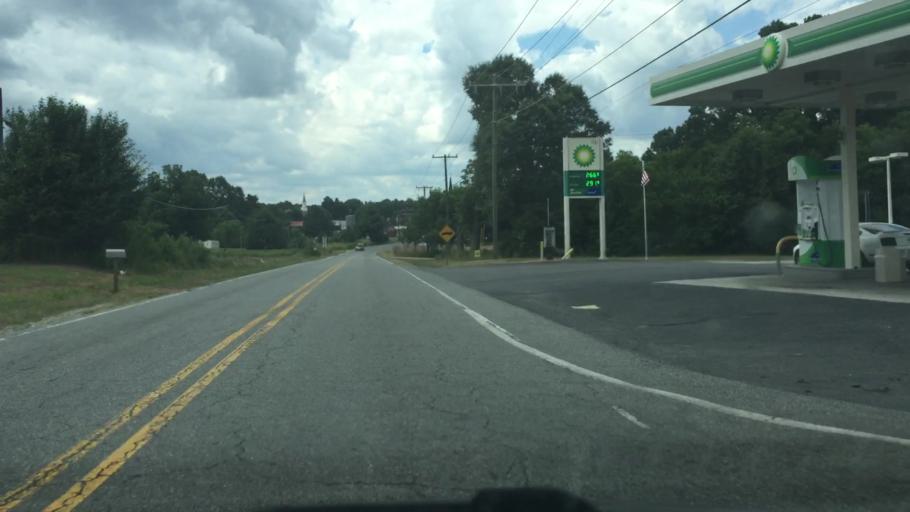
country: US
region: North Carolina
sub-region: Rowan County
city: Enochville
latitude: 35.5341
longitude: -80.6658
